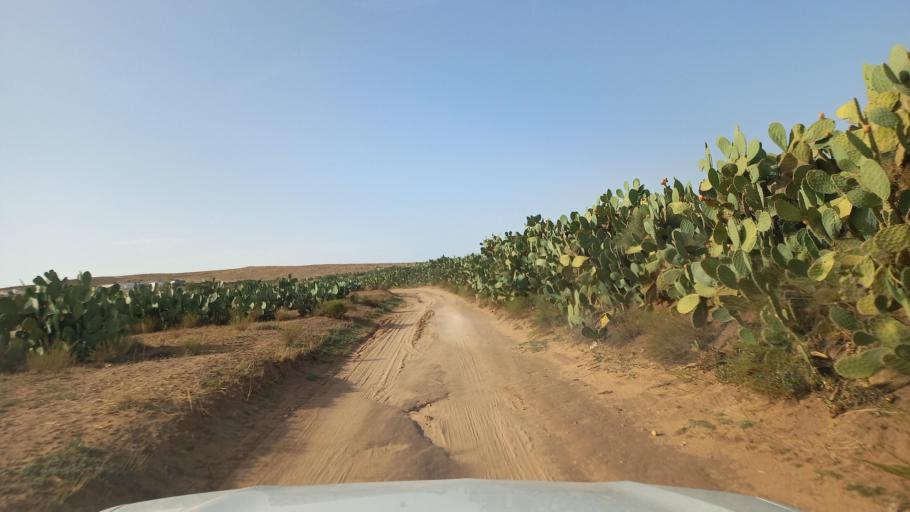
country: TN
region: Al Qasrayn
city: Kasserine
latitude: 35.3607
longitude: 8.8511
